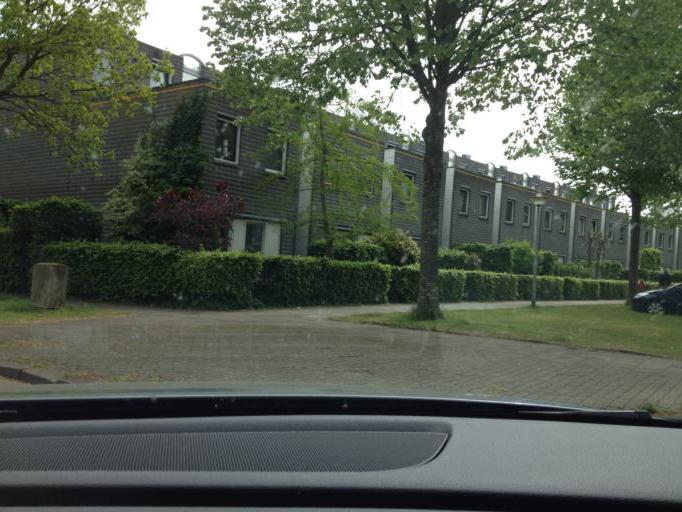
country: NL
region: Flevoland
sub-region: Gemeente Almere
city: Almere Stad
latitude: 52.3699
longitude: 5.2326
